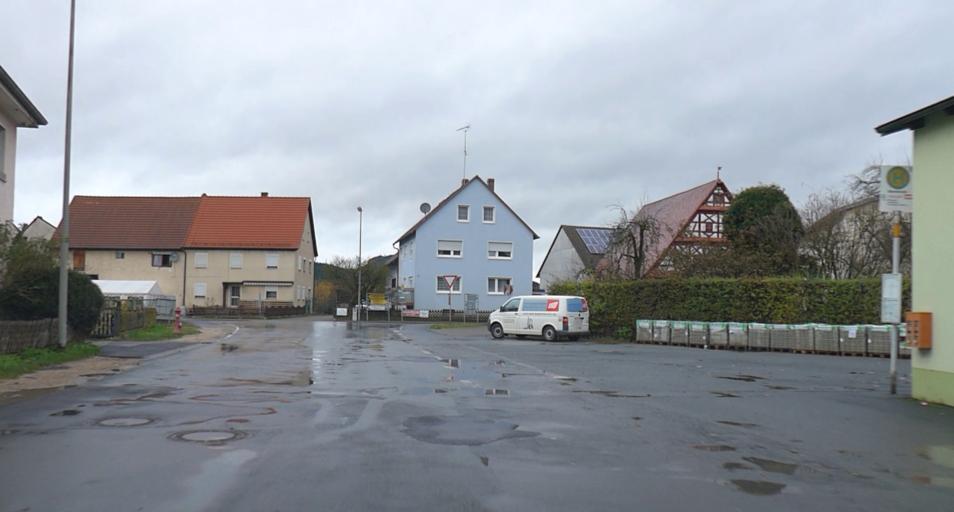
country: DE
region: Bavaria
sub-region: Upper Franconia
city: Leutenbach
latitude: 49.6896
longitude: 11.1705
